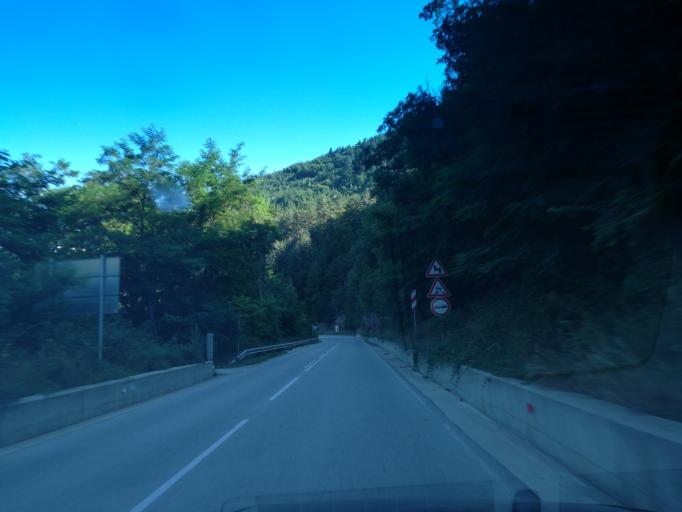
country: BG
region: Smolyan
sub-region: Obshtina Chepelare
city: Chepelare
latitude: 41.8375
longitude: 24.6797
